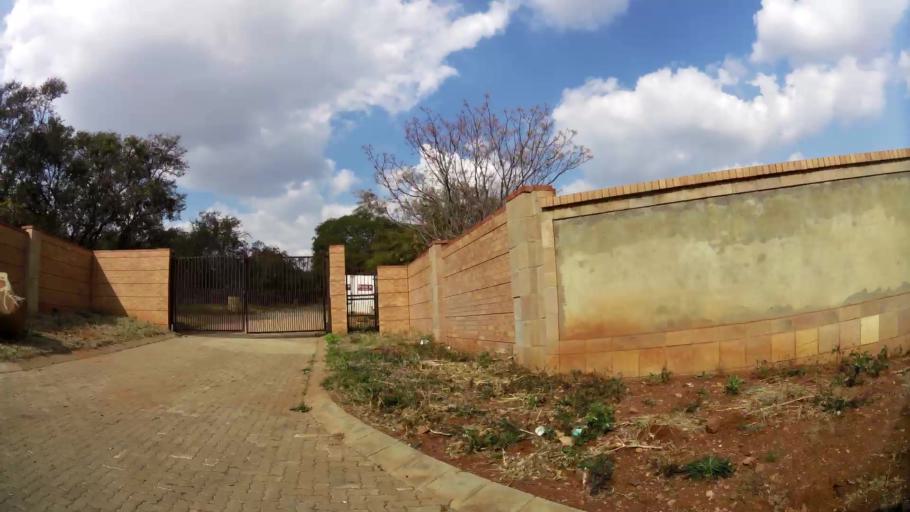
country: ZA
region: Gauteng
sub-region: City of Tshwane Metropolitan Municipality
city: Pretoria
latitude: -25.8011
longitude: 28.3440
